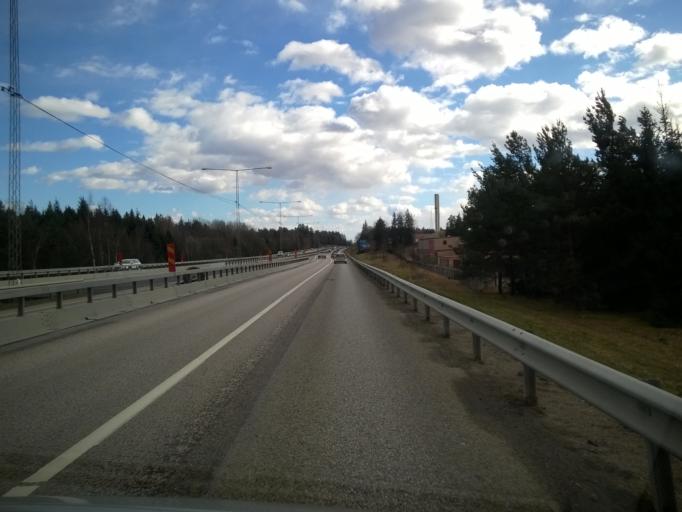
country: SE
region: Stockholm
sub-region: Jarfalla Kommun
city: Jakobsberg
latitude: 59.4323
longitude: 17.8464
